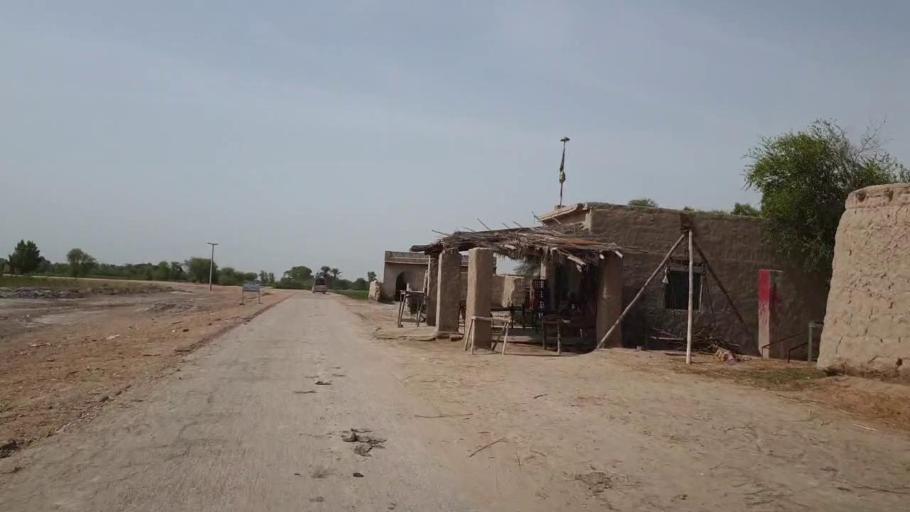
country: PK
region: Sindh
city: Bandhi
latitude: 26.5693
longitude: 68.3805
